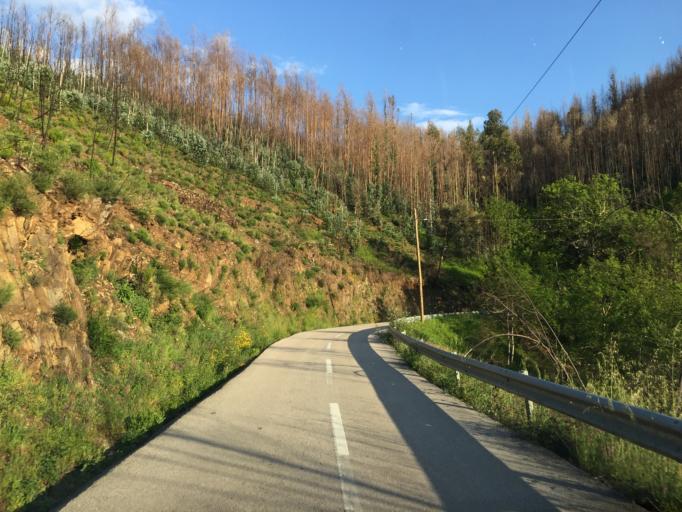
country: PT
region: Coimbra
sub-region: Arganil
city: Arganil
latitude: 40.1306
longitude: -8.0075
